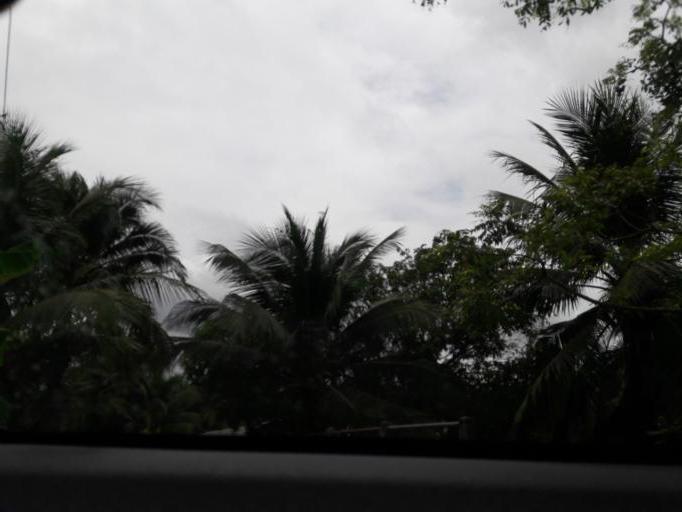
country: TH
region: Ratchaburi
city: Damnoen Saduak
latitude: 13.5682
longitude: 99.9995
